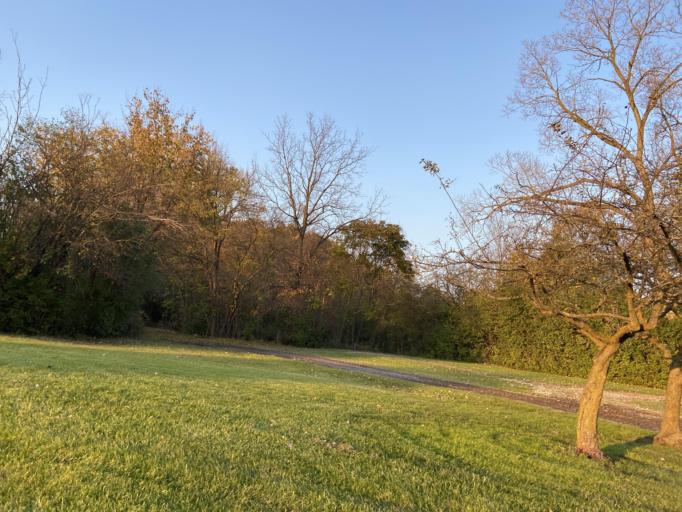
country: US
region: Michigan
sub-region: Wayne County
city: Redford
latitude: 42.4167
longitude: -83.3265
